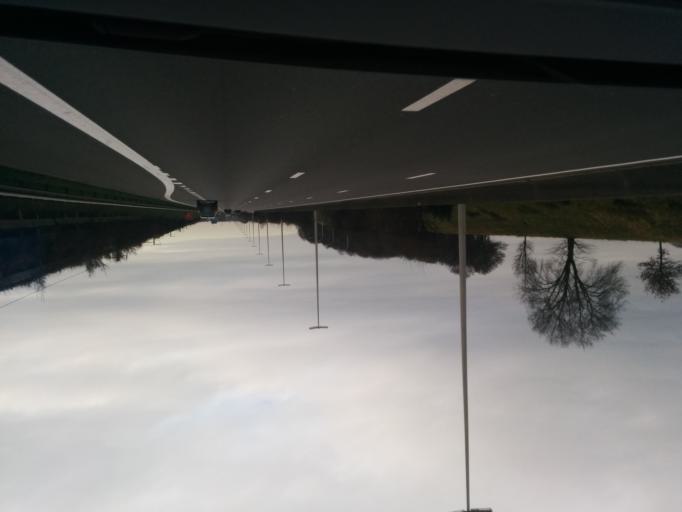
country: BE
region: Flanders
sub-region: Provincie Vlaams-Brabant
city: Boutersem
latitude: 50.8289
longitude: 4.8039
